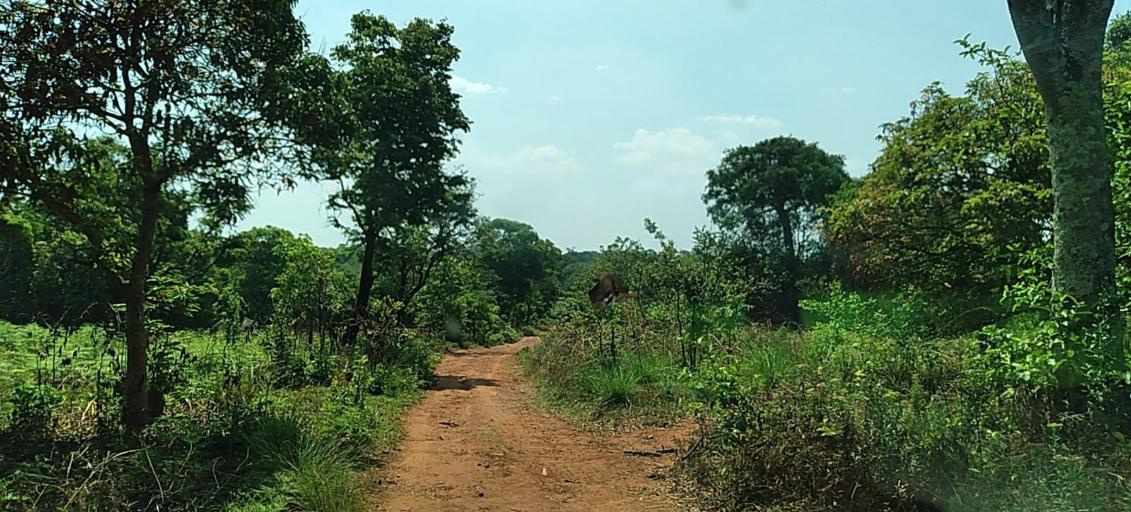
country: CD
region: Katanga
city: Kolwezi
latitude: -11.2806
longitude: 25.1362
